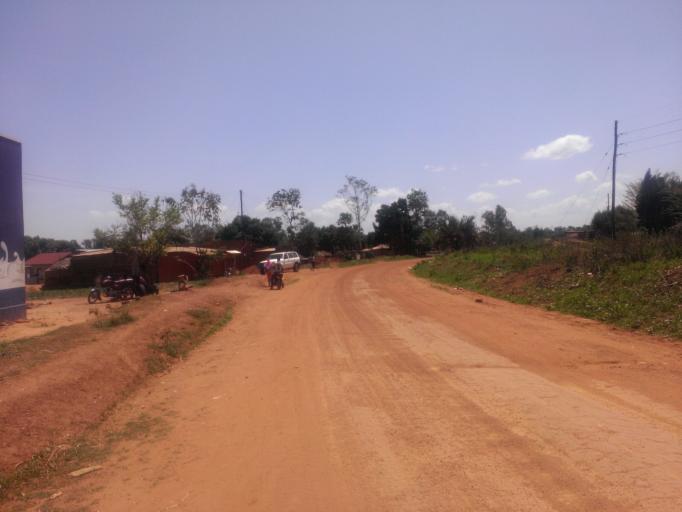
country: UG
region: Northern Region
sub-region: Gulu District
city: Gulu
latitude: 2.7859
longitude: 32.2961
